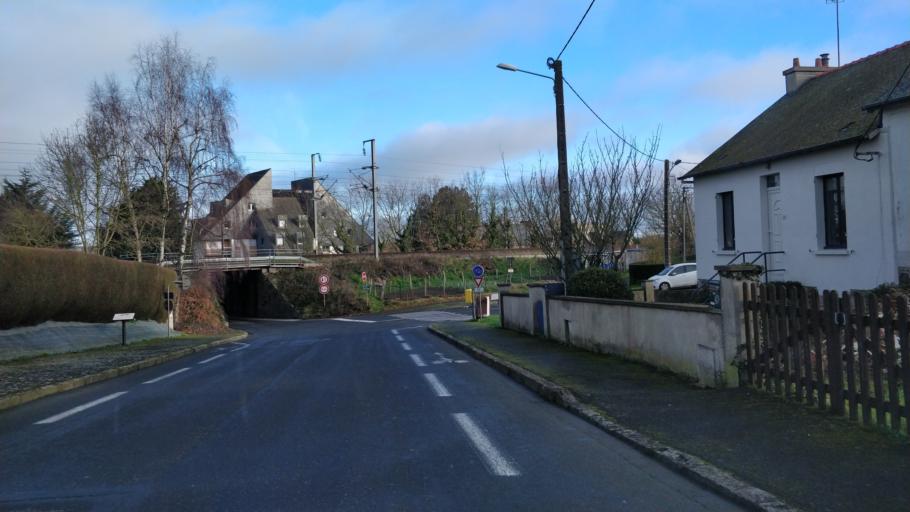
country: FR
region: Brittany
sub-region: Departement des Cotes-d'Armor
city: Lamballe
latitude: 48.4647
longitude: -2.5290
